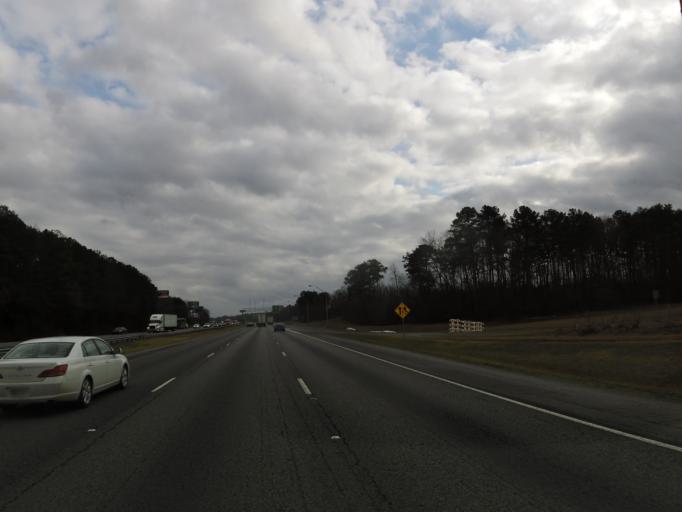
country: US
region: Georgia
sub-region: Gordon County
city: Calhoun
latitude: 34.5644
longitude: -84.9421
